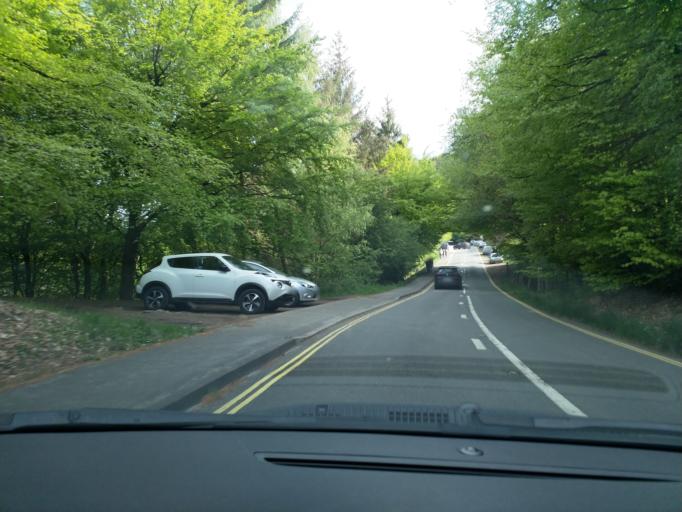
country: GB
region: England
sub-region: Derbyshire
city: Hope Valley
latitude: 53.3864
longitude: -1.7203
